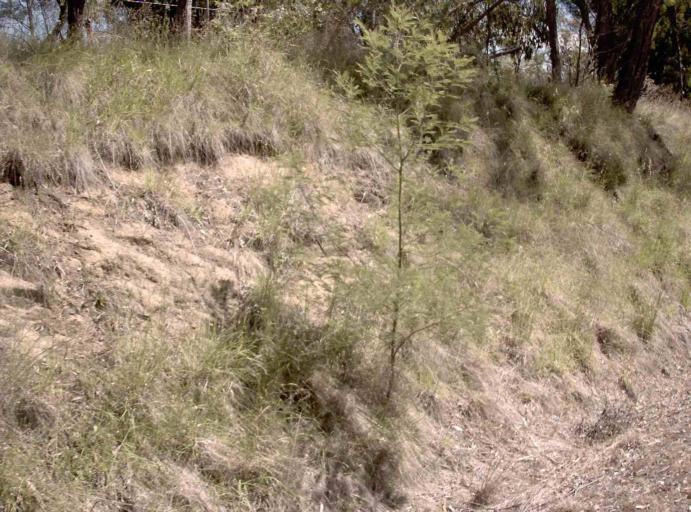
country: AU
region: Victoria
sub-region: East Gippsland
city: Lakes Entrance
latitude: -37.3374
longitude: 148.2302
